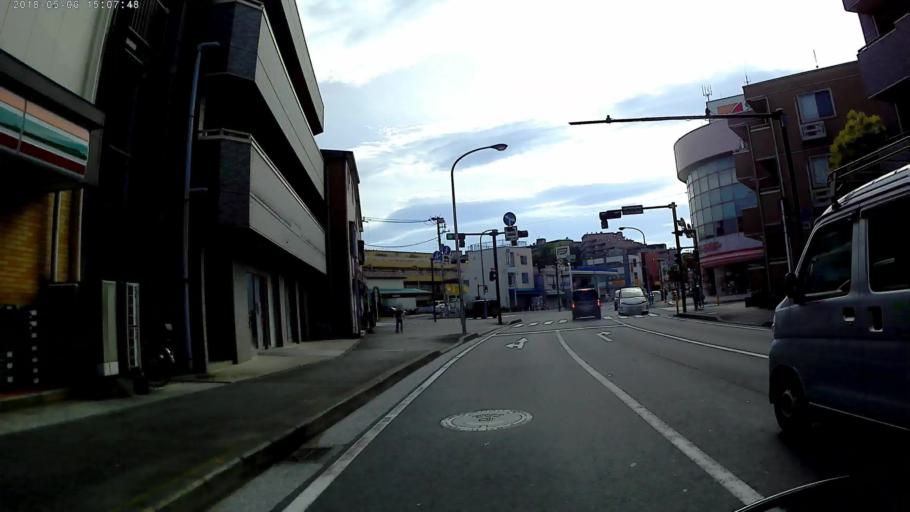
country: JP
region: Kanagawa
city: Yokohama
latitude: 35.4155
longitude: 139.5960
